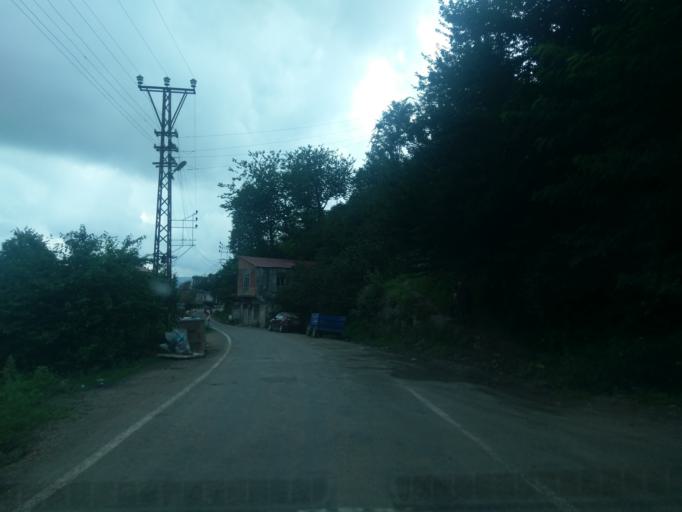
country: TR
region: Ordu
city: Camas
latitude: 40.8899
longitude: 37.6225
